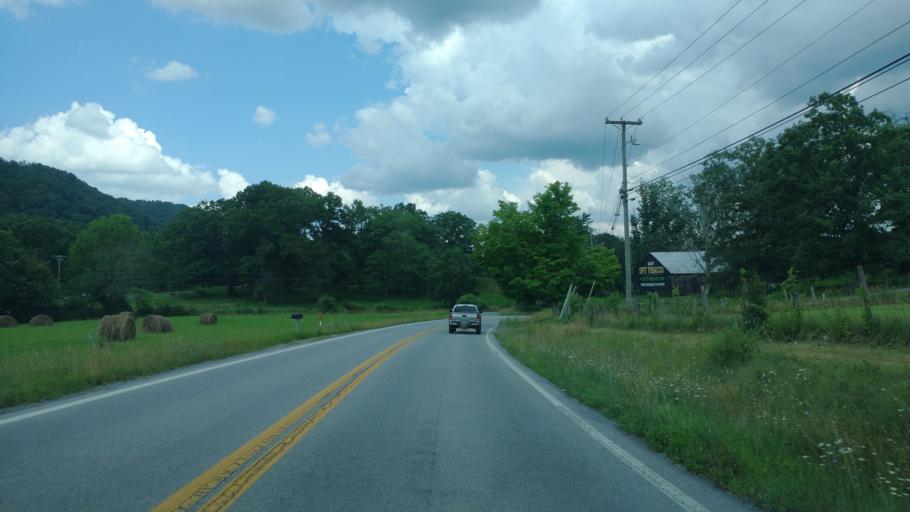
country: US
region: West Virginia
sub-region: Mercer County
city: Athens
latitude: 37.4483
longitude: -81.0033
